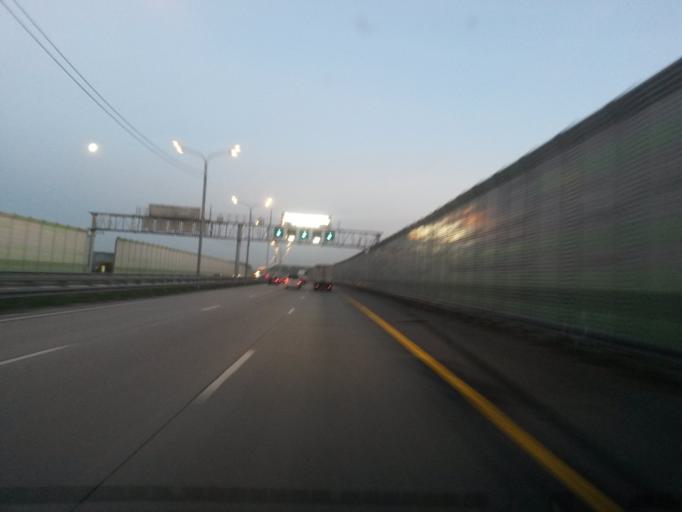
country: RU
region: Moskovskaya
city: Belyye Stolby
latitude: 55.3163
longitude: 37.8162
